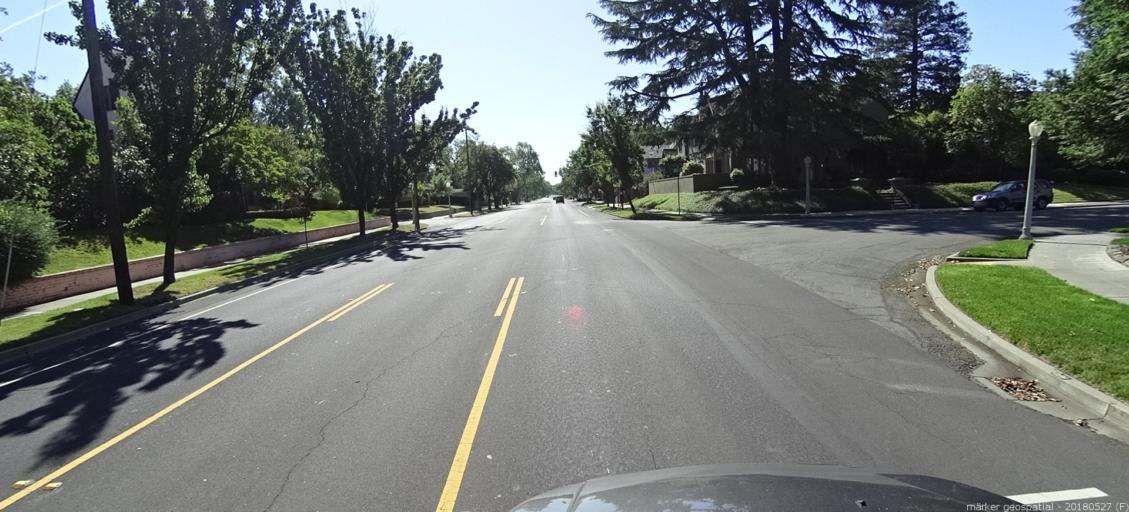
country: US
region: California
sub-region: Sacramento County
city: Sacramento
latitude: 38.5678
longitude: -121.4465
